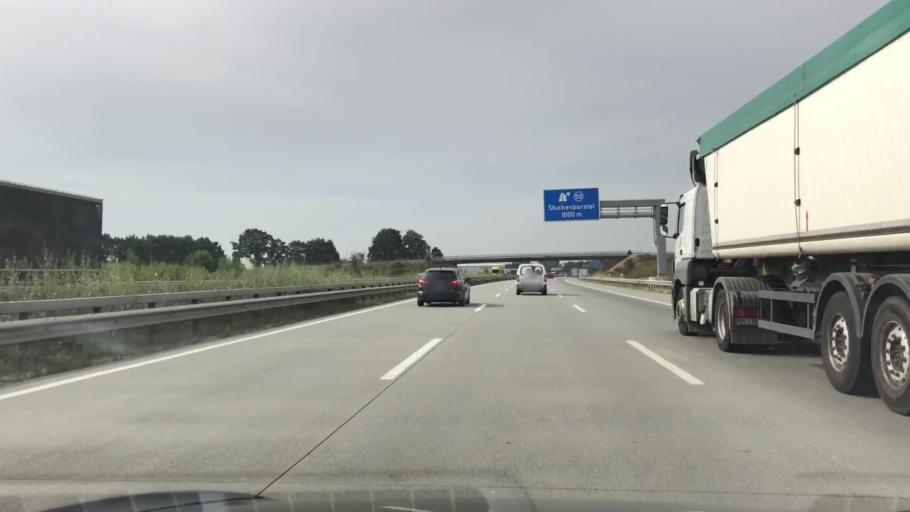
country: DE
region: Lower Saxony
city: Reessum
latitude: 53.1207
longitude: 9.2105
